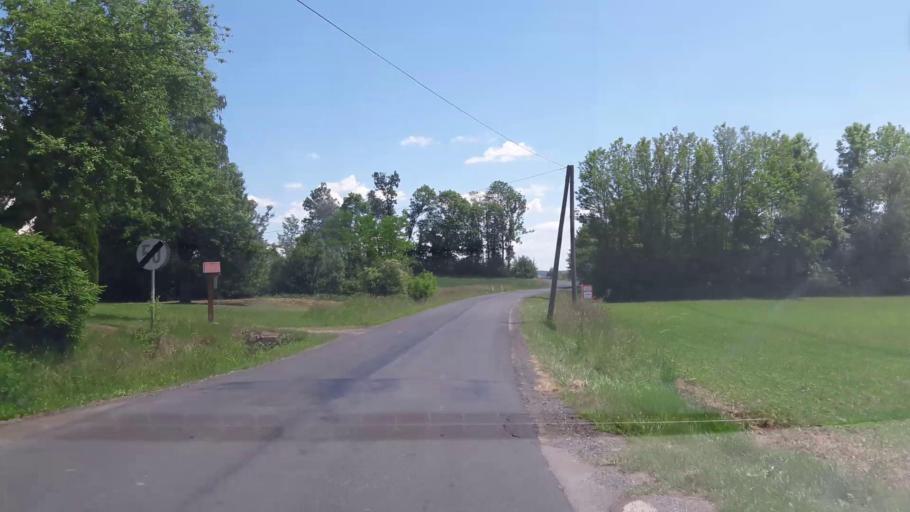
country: AT
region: Burgenland
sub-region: Politischer Bezirk Jennersdorf
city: Jennersdorf
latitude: 46.9592
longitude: 16.1112
